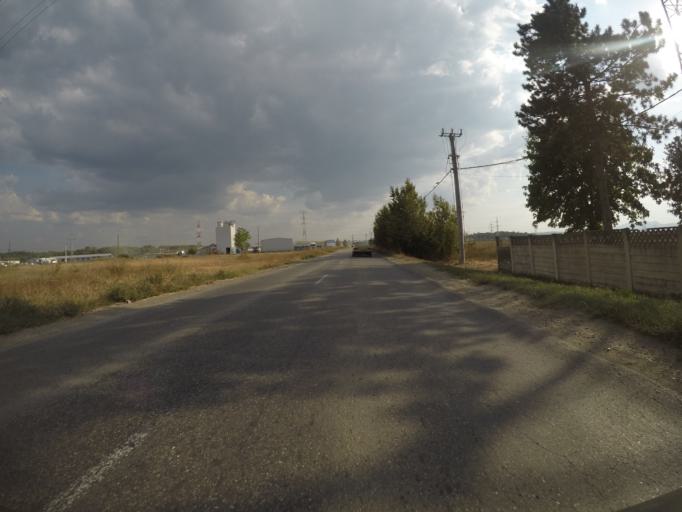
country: RO
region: Cluj
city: Turda
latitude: 46.5429
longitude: 23.7836
